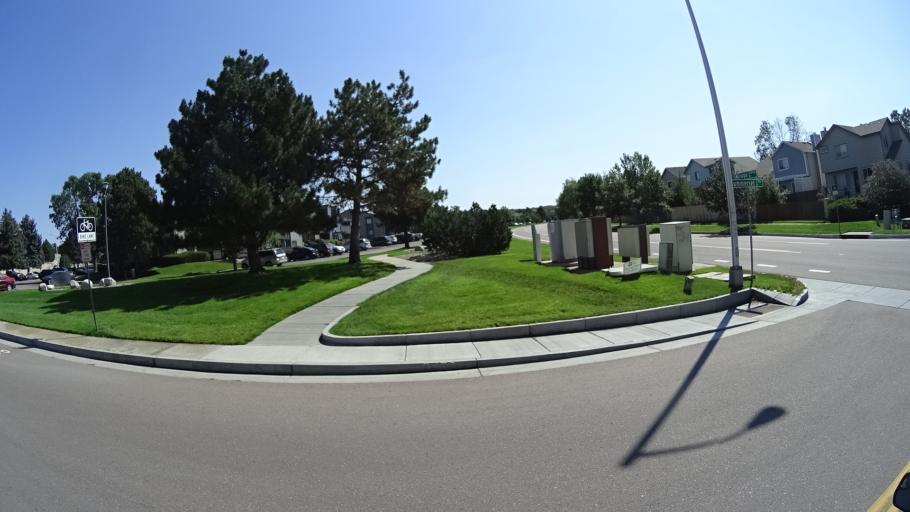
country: US
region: Colorado
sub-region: El Paso County
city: Air Force Academy
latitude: 38.9492
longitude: -104.7887
